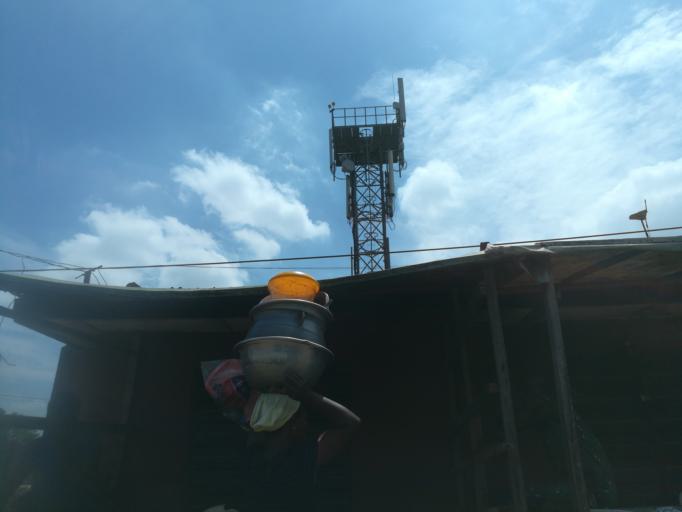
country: NG
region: Lagos
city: Oshodi
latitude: 6.5646
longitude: 3.3346
